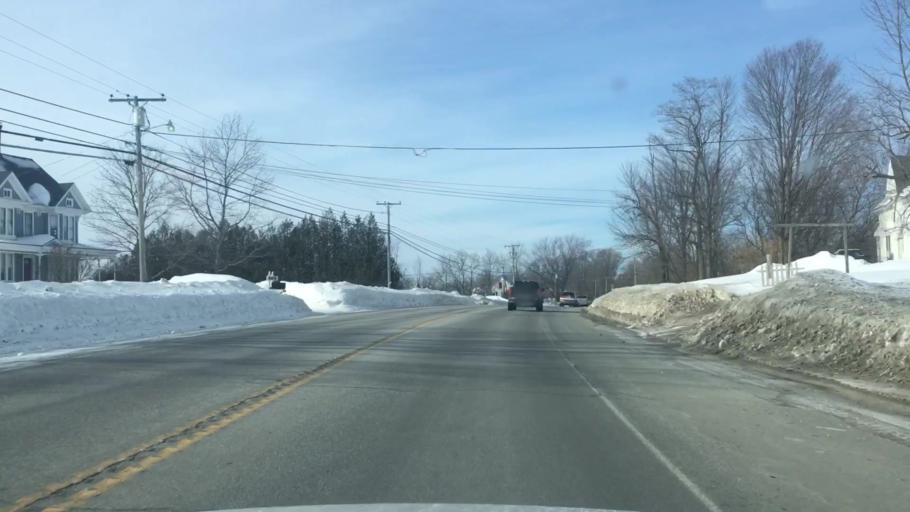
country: US
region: Maine
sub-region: Penobscot County
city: Charleston
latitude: 44.9927
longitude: -69.0183
